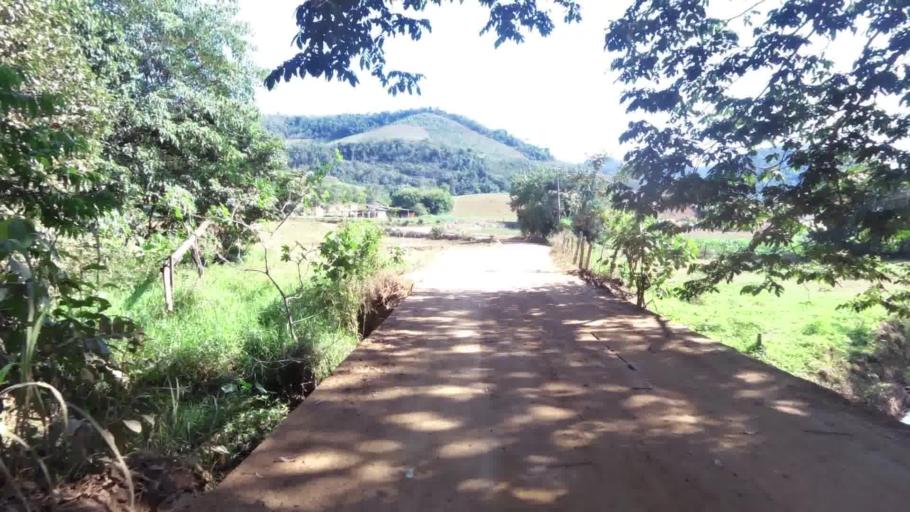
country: BR
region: Espirito Santo
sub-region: Alfredo Chaves
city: Alfredo Chaves
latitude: -20.5323
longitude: -40.8397
